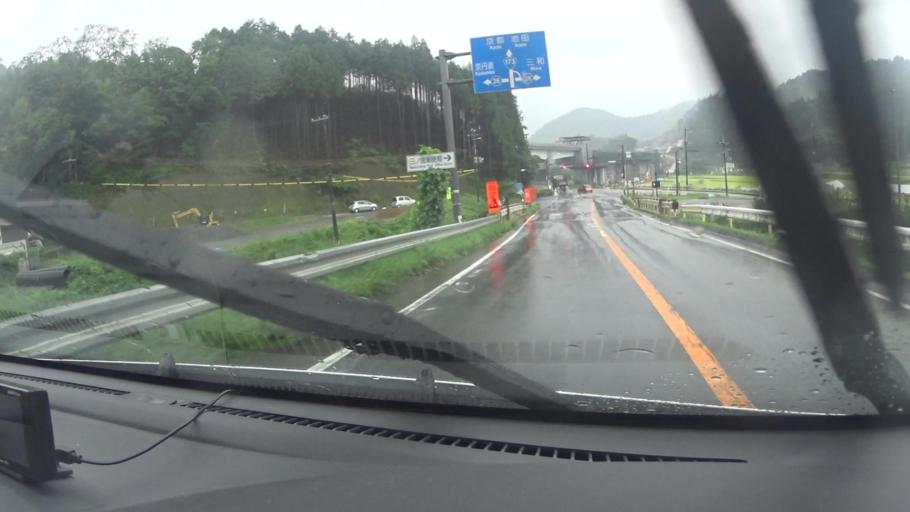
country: JP
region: Kyoto
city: Ayabe
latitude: 35.2208
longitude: 135.3413
